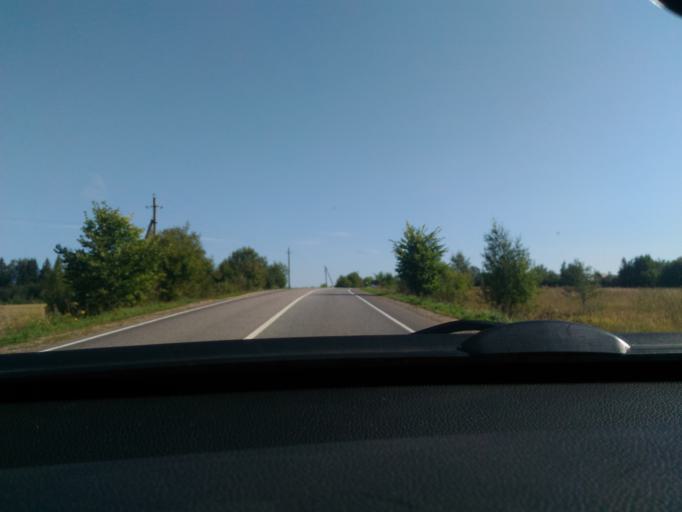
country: RU
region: Moskovskaya
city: Dedenevo
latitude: 56.2564
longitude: 37.5579
